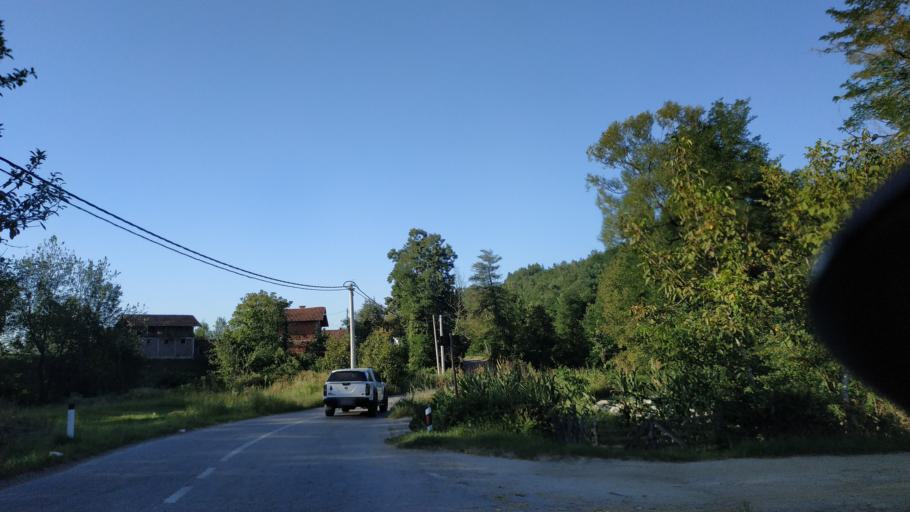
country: RS
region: Central Serbia
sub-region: Rasinski Okrug
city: Krusevac
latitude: 43.4776
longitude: 21.3544
